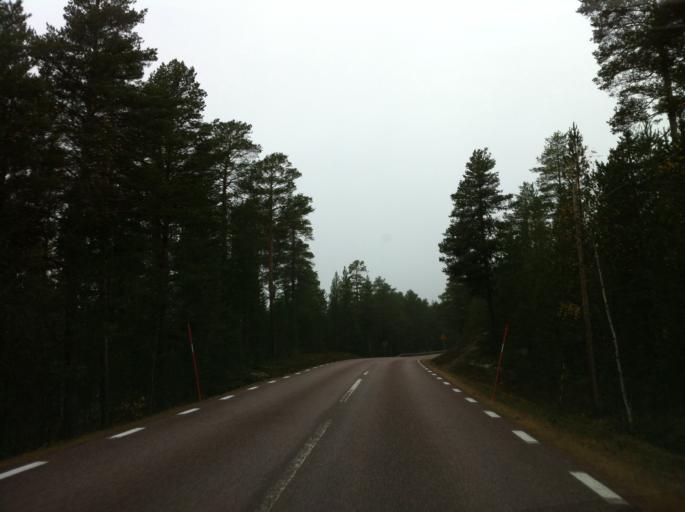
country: NO
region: Hedmark
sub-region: Trysil
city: Innbygda
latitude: 61.8461
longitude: 12.7740
